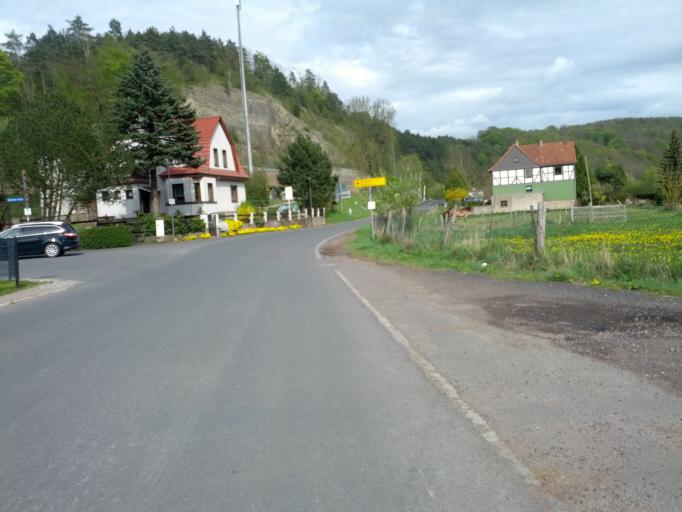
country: DE
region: Thuringia
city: Krauthausen
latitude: 51.0076
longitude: 10.2307
